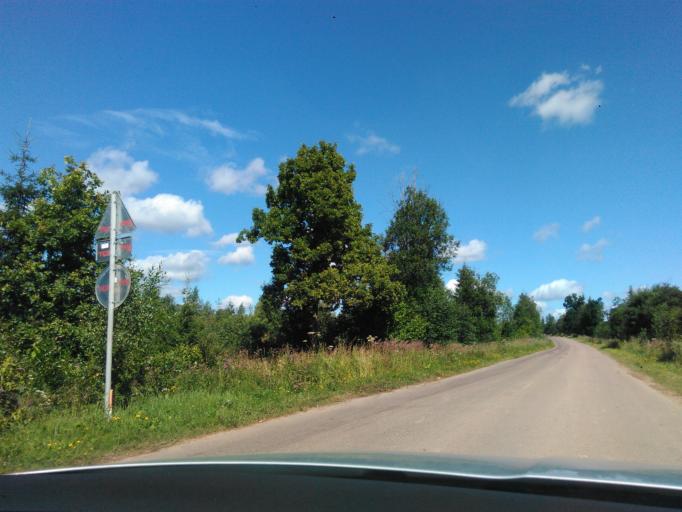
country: RU
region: Moskovskaya
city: Klin
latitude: 56.2103
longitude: 36.8100
